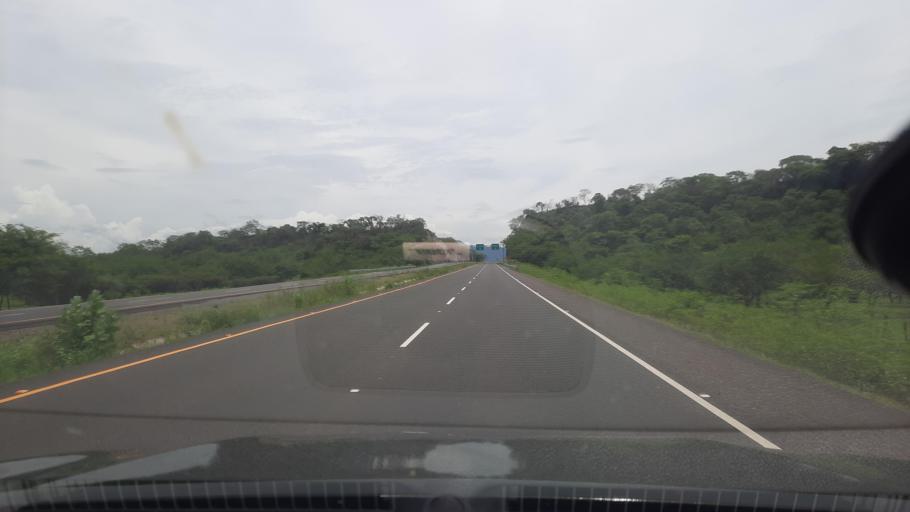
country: HN
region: Valle
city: Aramecina
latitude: 13.7327
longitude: -87.7184
